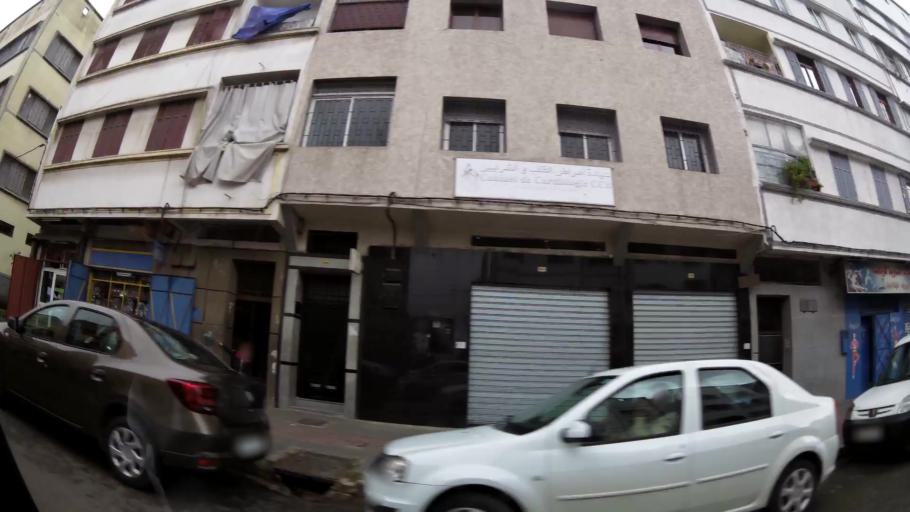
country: MA
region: Grand Casablanca
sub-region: Casablanca
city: Casablanca
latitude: 33.5441
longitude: -7.5762
